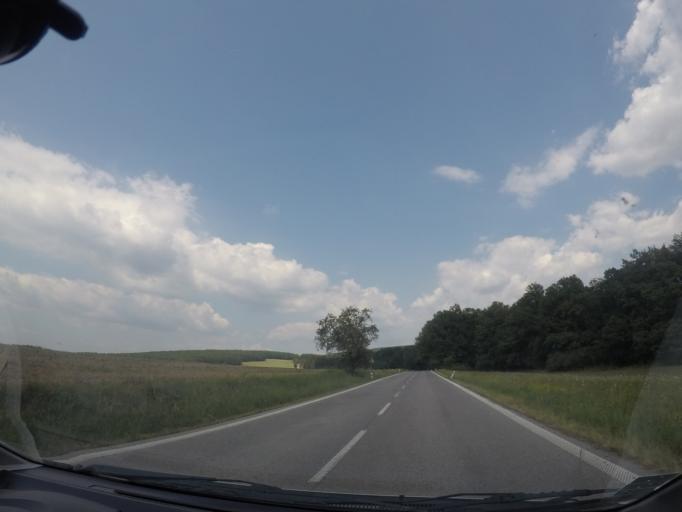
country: SK
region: Banskobystricky
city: Dudince
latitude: 48.2575
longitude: 18.7806
